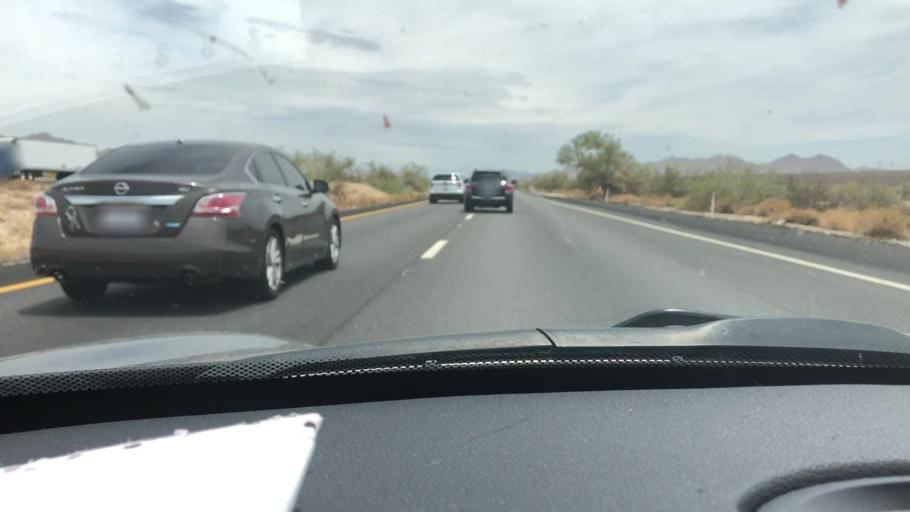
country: US
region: California
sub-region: Riverside County
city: Mecca
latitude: 33.6600
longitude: -115.7981
